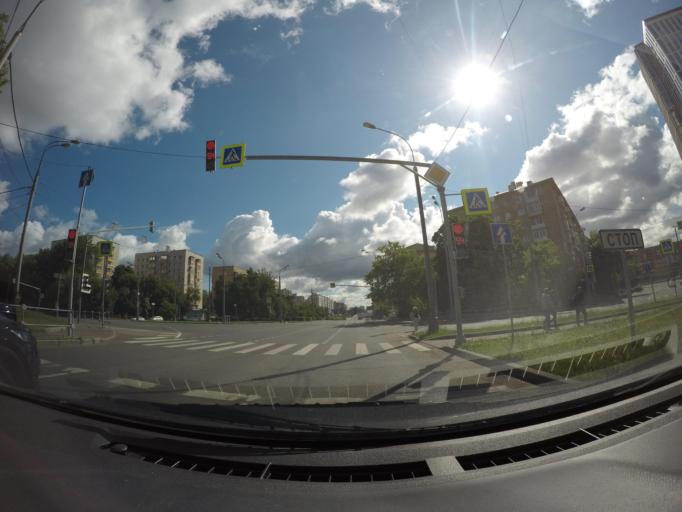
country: RU
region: Moskovskaya
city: Dorogomilovo
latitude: 55.7911
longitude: 37.5692
